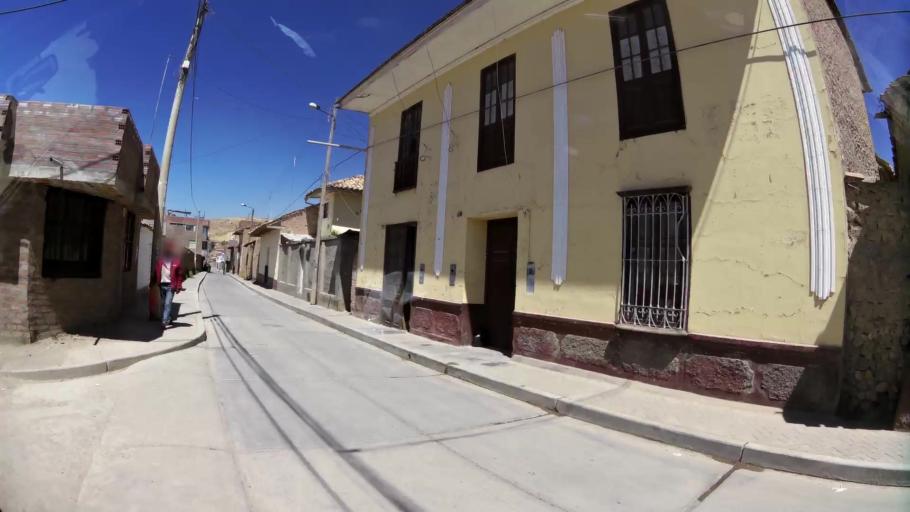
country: PE
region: Junin
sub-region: Provincia de Jauja
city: Jauja
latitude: -11.7783
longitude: -75.5010
